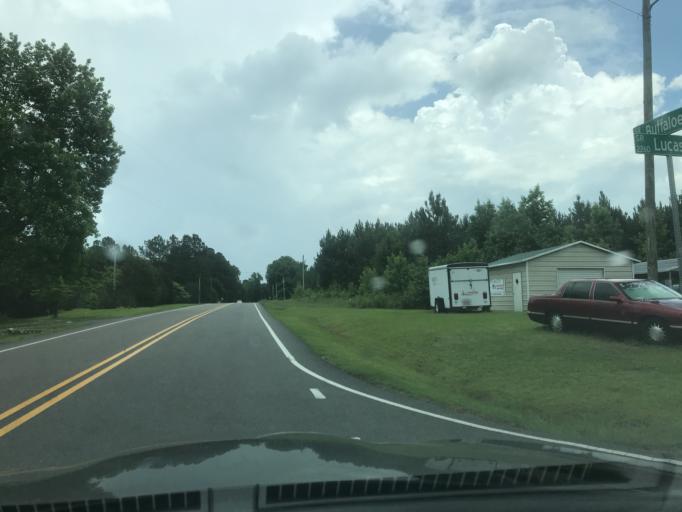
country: US
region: North Carolina
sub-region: Wake County
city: Knightdale
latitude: 35.8347
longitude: -78.4729
